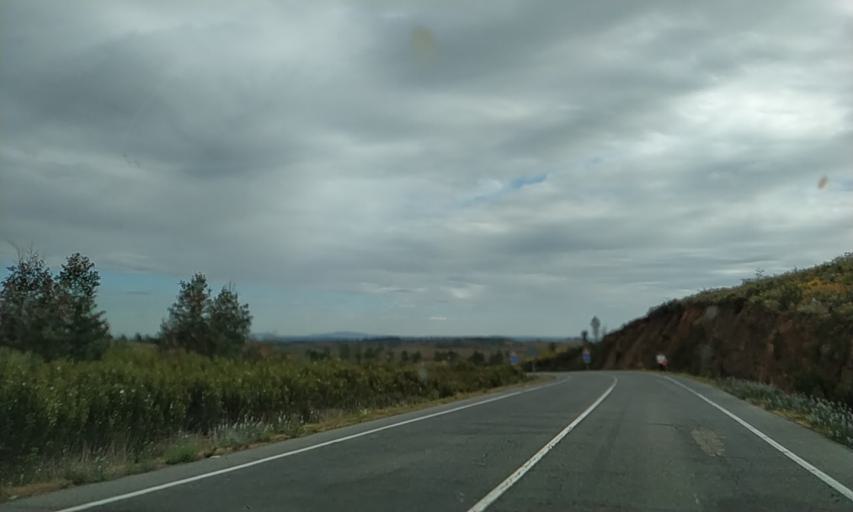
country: ES
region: Extremadura
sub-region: Provincia de Caceres
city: Perales del Puerto
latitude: 40.1806
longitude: -6.6753
